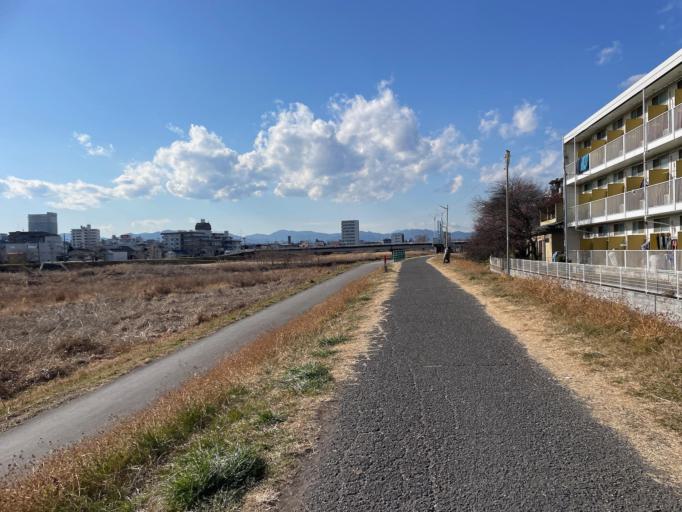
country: JP
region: Tokyo
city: Hachioji
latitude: 35.6648
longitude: 139.3440
